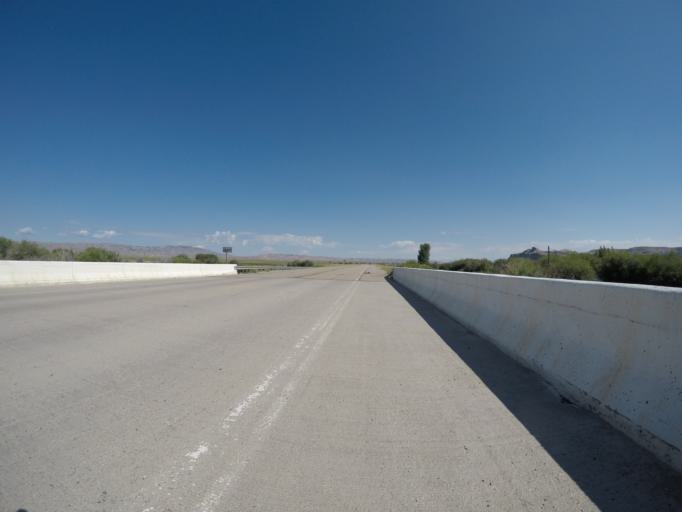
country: US
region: Wyoming
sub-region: Sublette County
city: Marbleton
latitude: 42.2276
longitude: -110.1921
